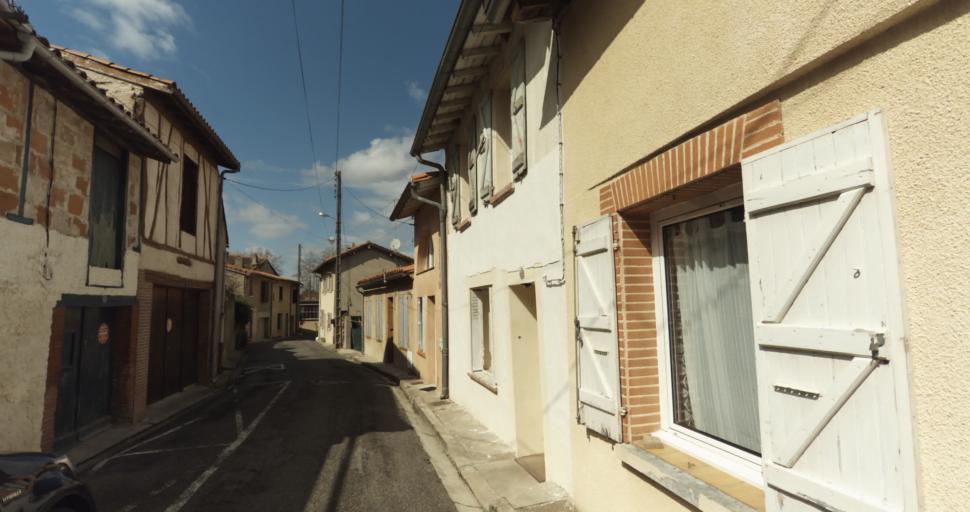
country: FR
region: Midi-Pyrenees
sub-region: Departement de la Haute-Garonne
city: Auterive
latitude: 43.3533
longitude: 1.4790
